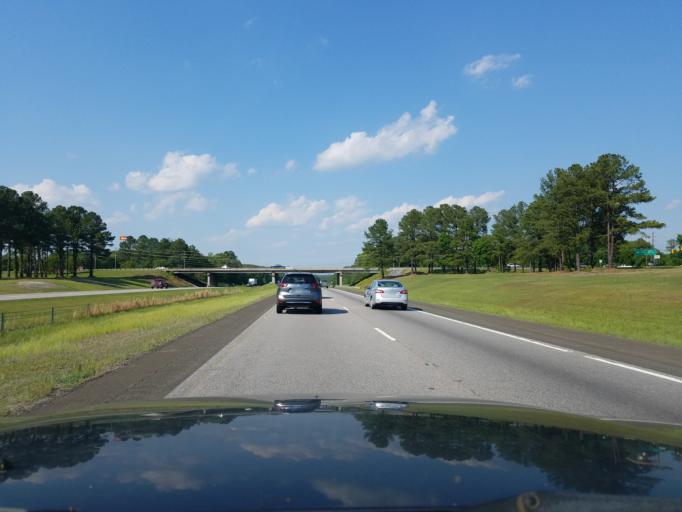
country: US
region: North Carolina
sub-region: Granville County
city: Butner
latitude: 36.1460
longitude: -78.7261
